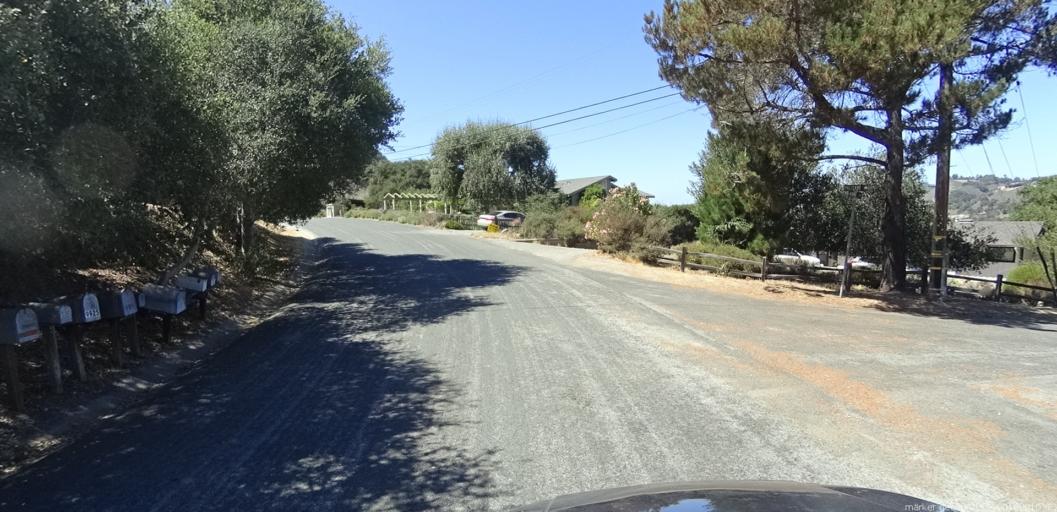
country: US
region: California
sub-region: Monterey County
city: Carmel Valley Village
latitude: 36.5158
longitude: -121.8024
